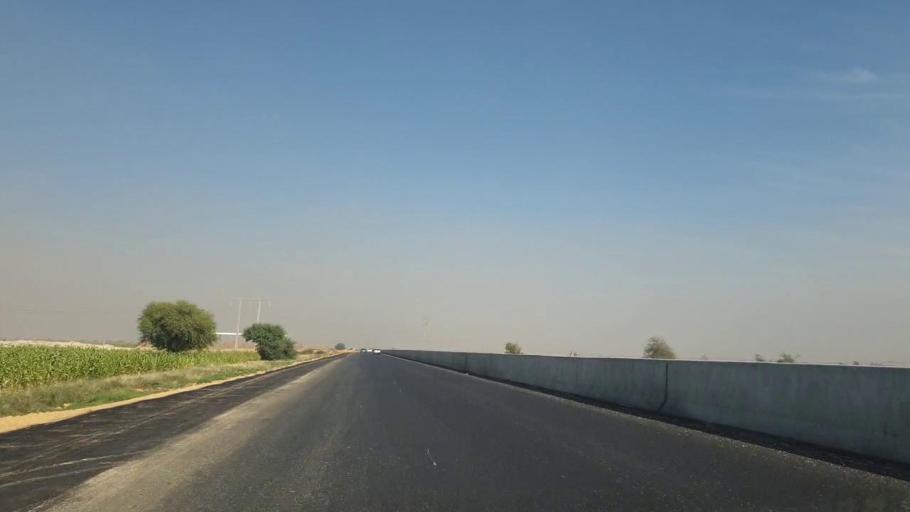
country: PK
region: Sindh
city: Jamshoro
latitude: 25.5327
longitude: 68.2825
